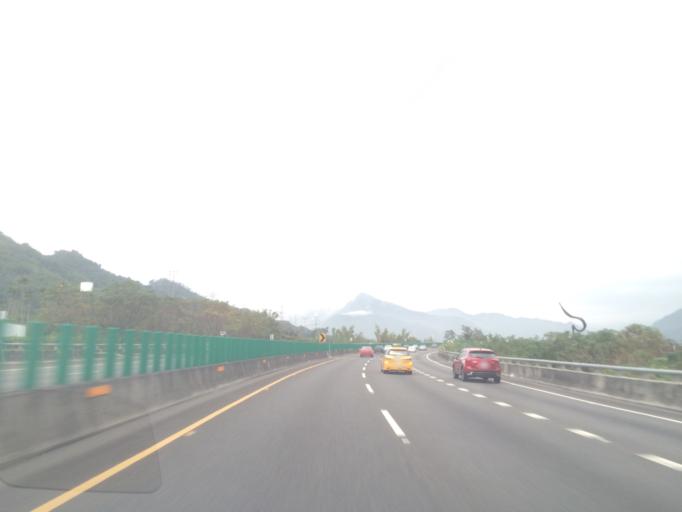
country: TW
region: Taiwan
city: Zhongxing New Village
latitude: 23.9960
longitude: 120.8014
